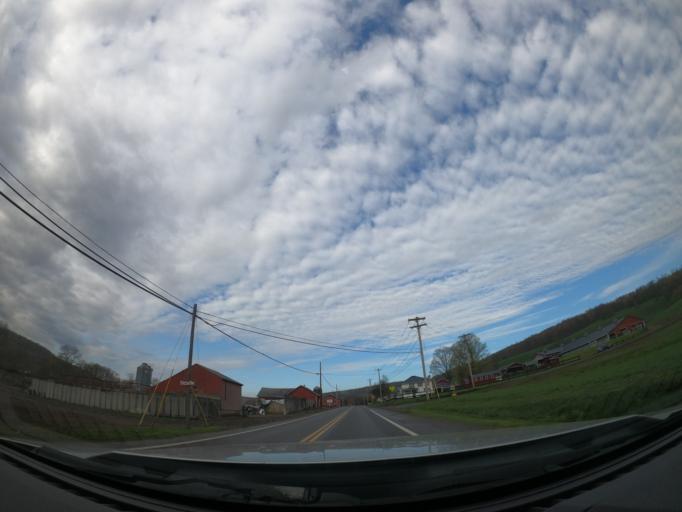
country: US
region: New York
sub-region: Cortland County
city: McGraw
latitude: 42.6725
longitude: -76.0851
